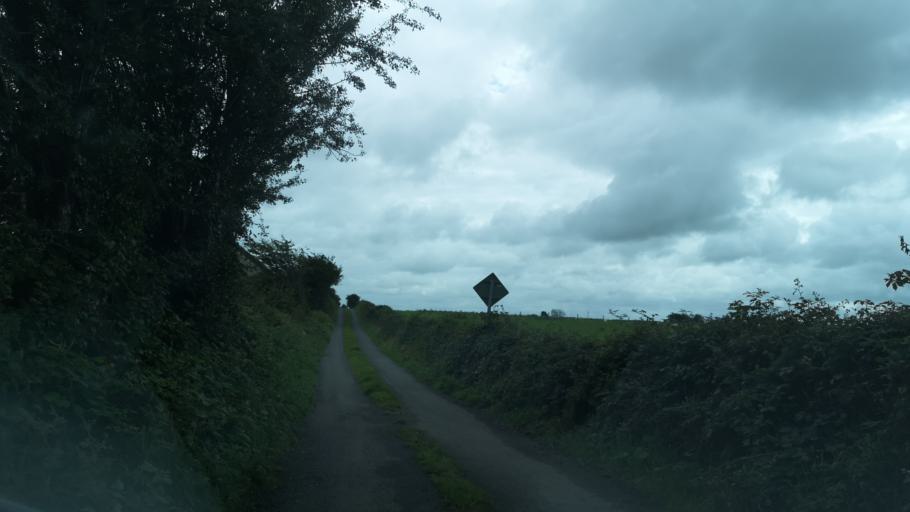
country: IE
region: Connaught
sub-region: County Galway
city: Athenry
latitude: 53.2854
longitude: -8.7158
